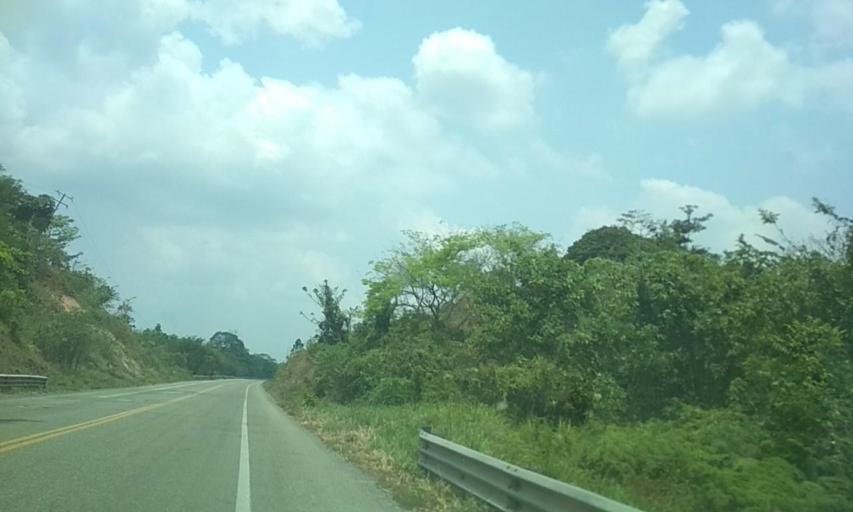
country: MX
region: Tabasco
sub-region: Huimanguillo
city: Francisco Rueda
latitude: 17.6481
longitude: -93.8328
